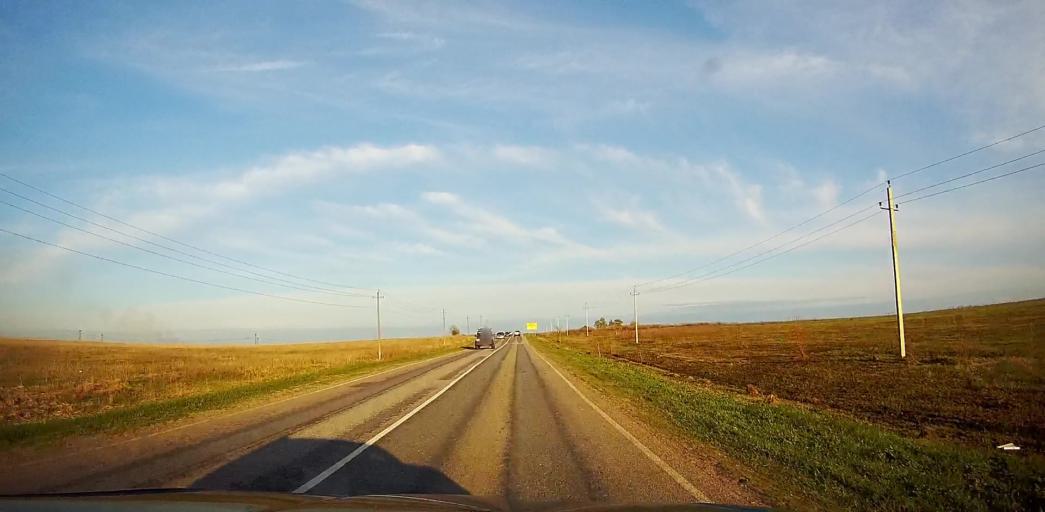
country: RU
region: Moskovskaya
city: Meshcherino
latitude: 55.2696
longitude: 38.2431
